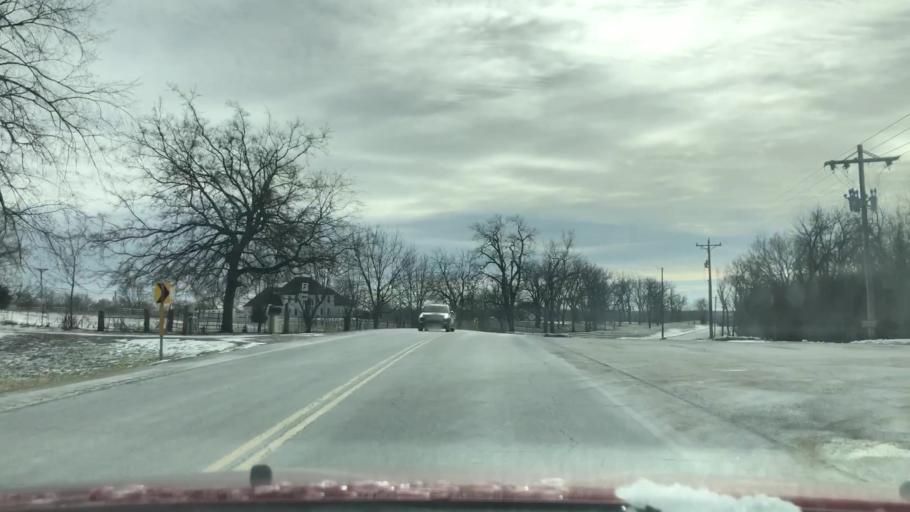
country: US
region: Missouri
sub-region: Jackson County
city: Oak Grove
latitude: 38.9336
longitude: -94.1328
